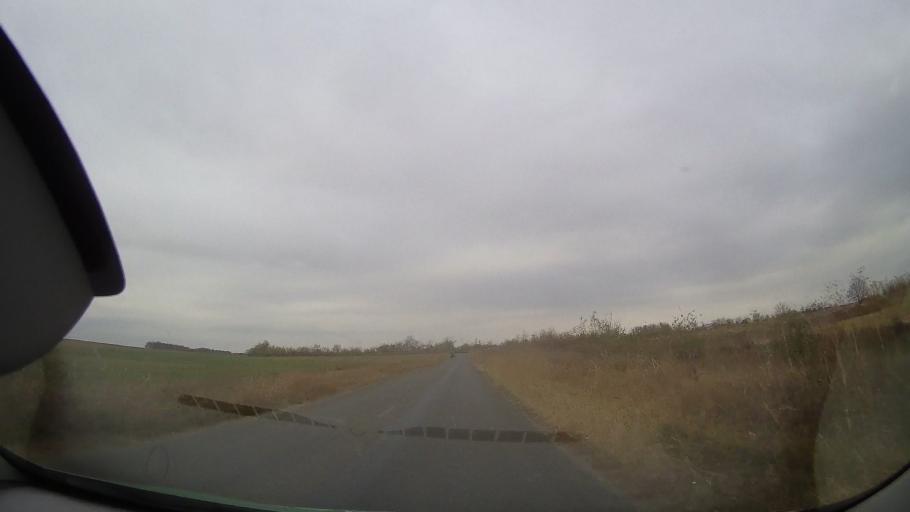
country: RO
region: Buzau
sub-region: Comuna Largu
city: Largu
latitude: 44.9692
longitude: 27.1849
